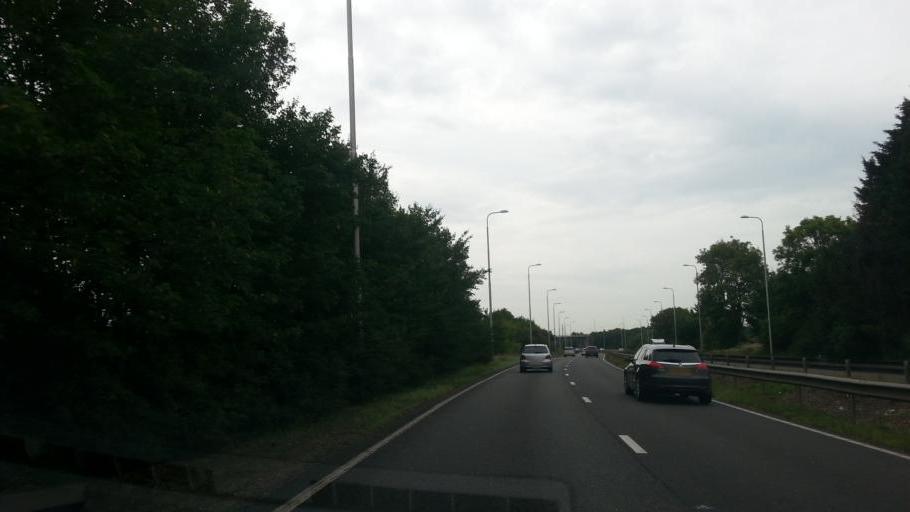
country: GB
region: England
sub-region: Central Bedfordshire
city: Tempsford
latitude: 52.1623
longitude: -0.3007
